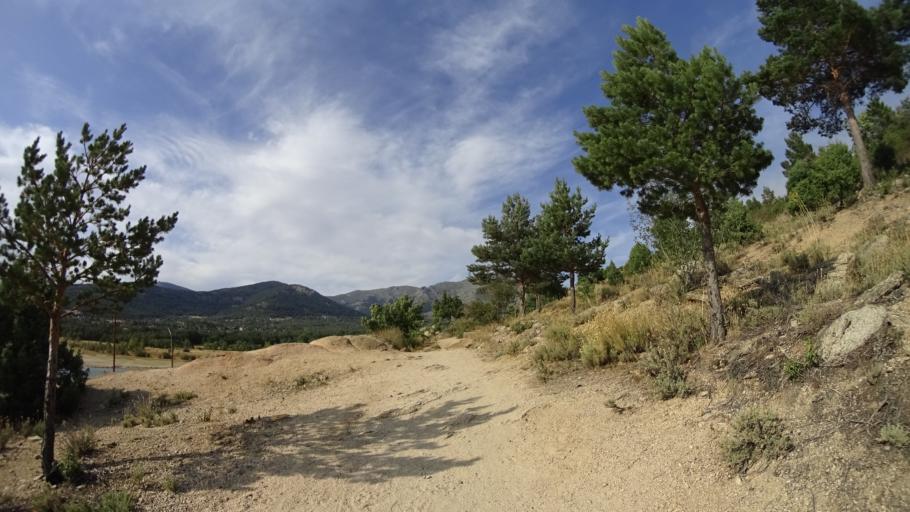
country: ES
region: Madrid
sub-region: Provincia de Madrid
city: Becerril de la Sierra
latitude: 40.7195
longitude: -4.0033
